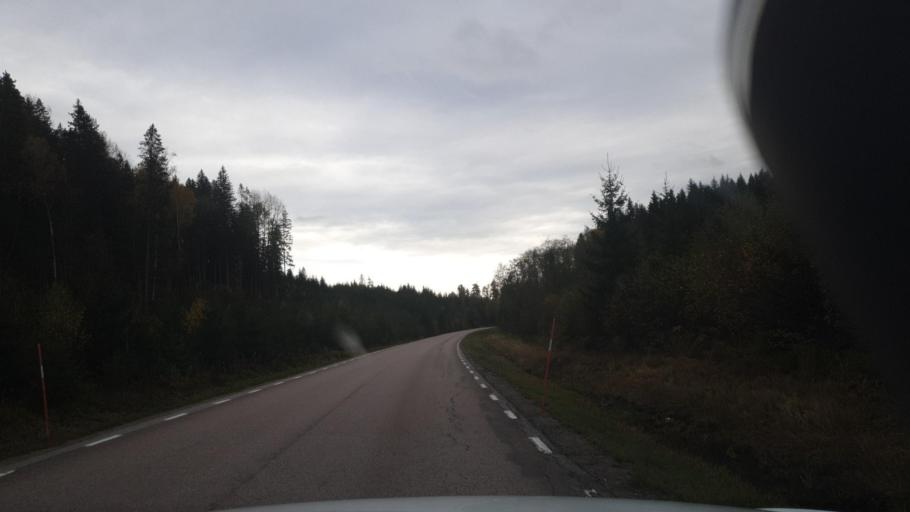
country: SE
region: Vaermland
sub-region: Arvika Kommun
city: Arvika
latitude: 59.6798
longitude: 12.7933
